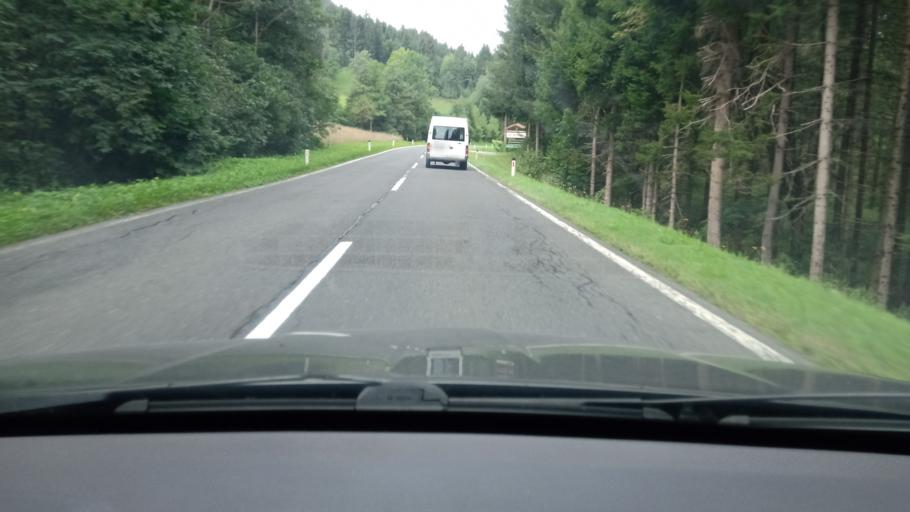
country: AT
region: Carinthia
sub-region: Politischer Bezirk Hermagor
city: Hermagor
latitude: 46.6486
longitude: 13.3313
